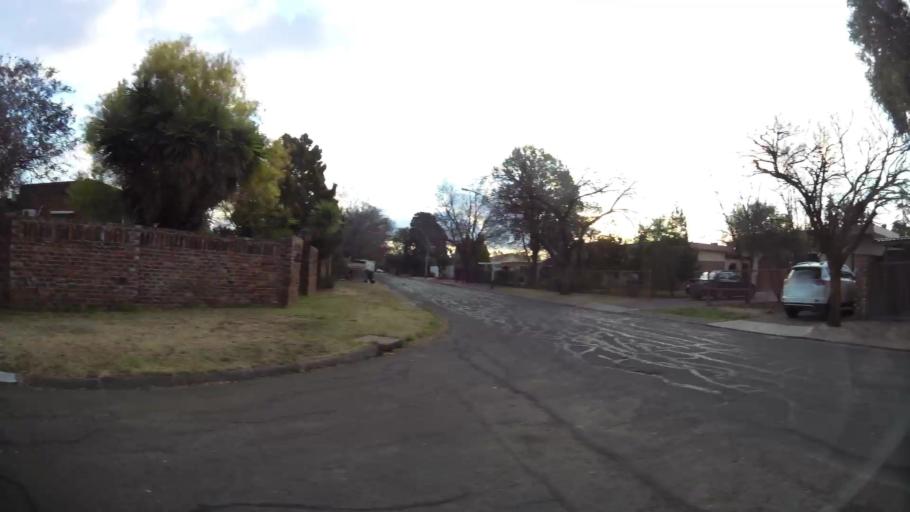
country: ZA
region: Orange Free State
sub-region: Mangaung Metropolitan Municipality
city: Bloemfontein
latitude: -29.1385
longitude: 26.1724
